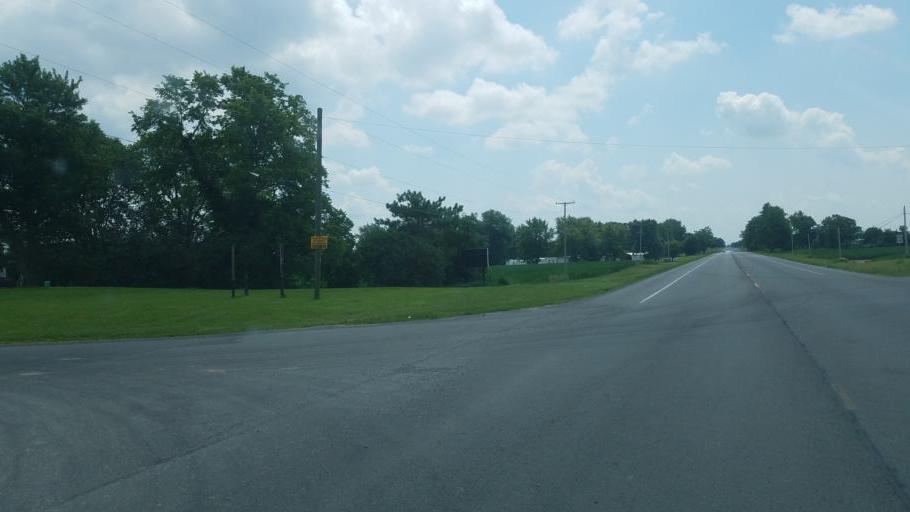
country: US
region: Ohio
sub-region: Hardin County
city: Kenton
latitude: 40.5920
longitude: -83.6408
